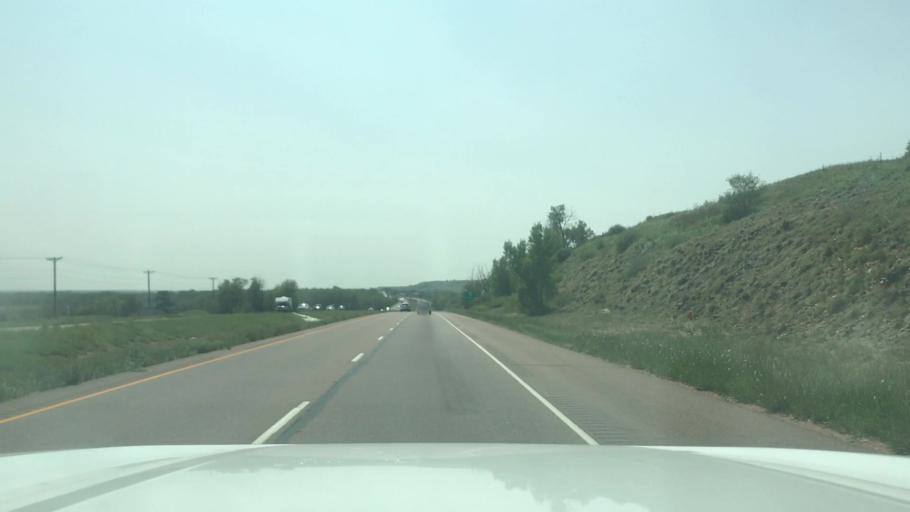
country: US
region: Colorado
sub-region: El Paso County
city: Fountain
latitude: 38.6900
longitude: -104.7187
